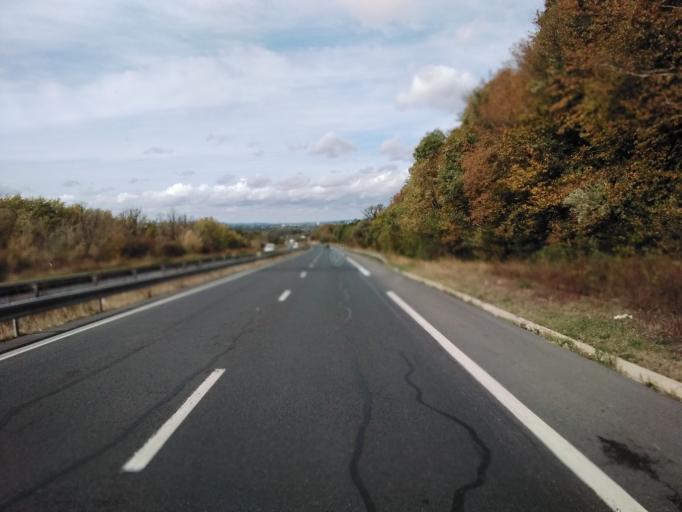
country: FR
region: Champagne-Ardenne
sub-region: Departement des Ardennes
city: Lumes
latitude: 49.7352
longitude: 4.7962
